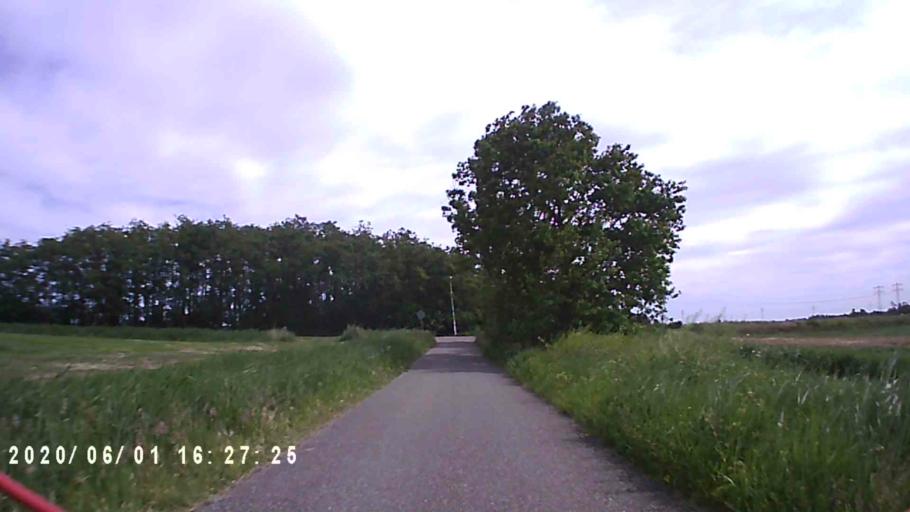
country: NL
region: Friesland
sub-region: Gemeente Leeuwarden
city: Camminghaburen
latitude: 53.1916
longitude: 5.8638
